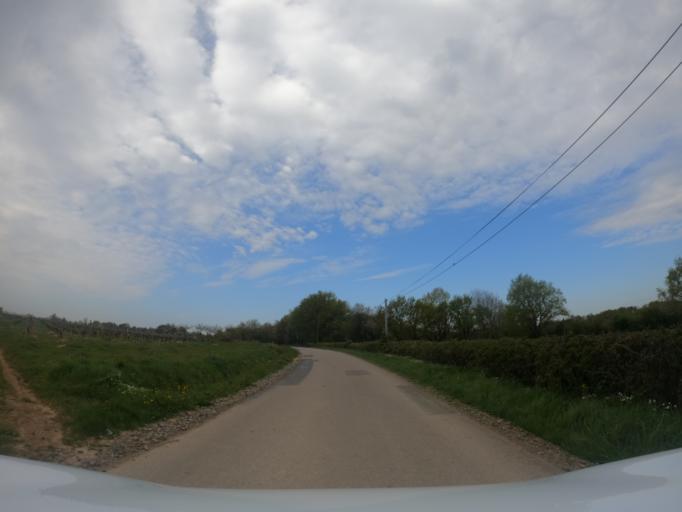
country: FR
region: Pays de la Loire
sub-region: Departement de la Vendee
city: Le Champ-Saint-Pere
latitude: 46.5329
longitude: -1.3340
